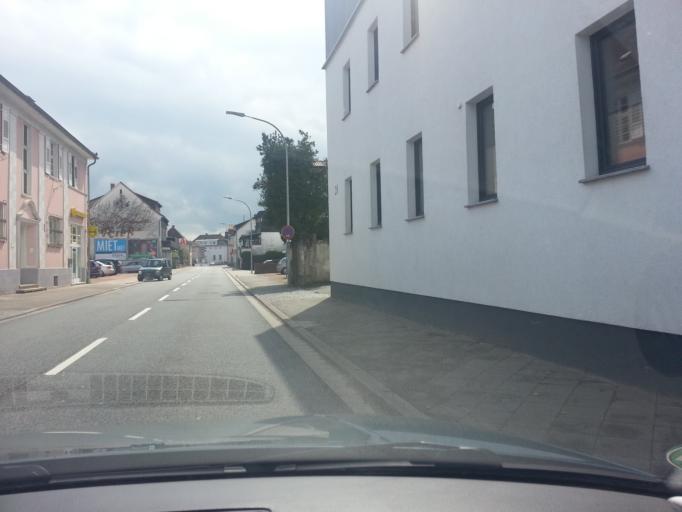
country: DE
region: Saarland
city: Blieskastel
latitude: 49.2423
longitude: 7.2597
